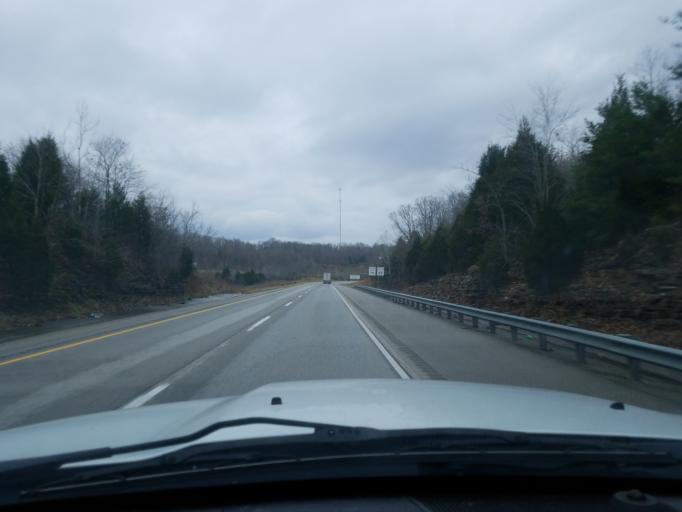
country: US
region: Indiana
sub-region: Crawford County
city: English
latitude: 38.2386
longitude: -86.3701
